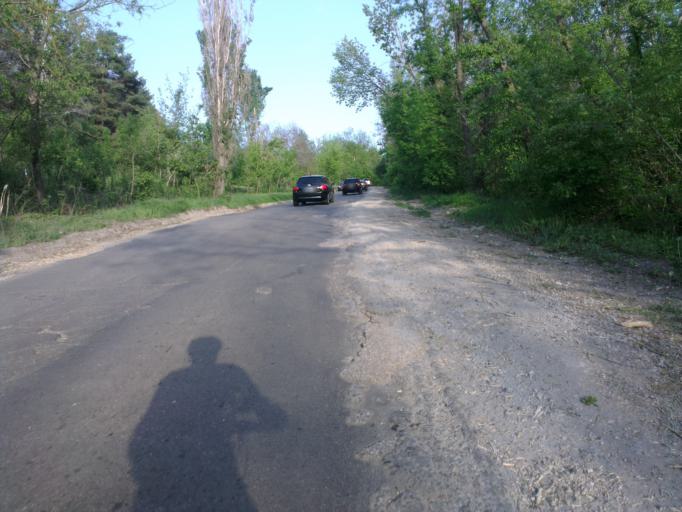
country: MD
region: Chisinau
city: Stauceni
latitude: 47.0608
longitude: 28.8843
